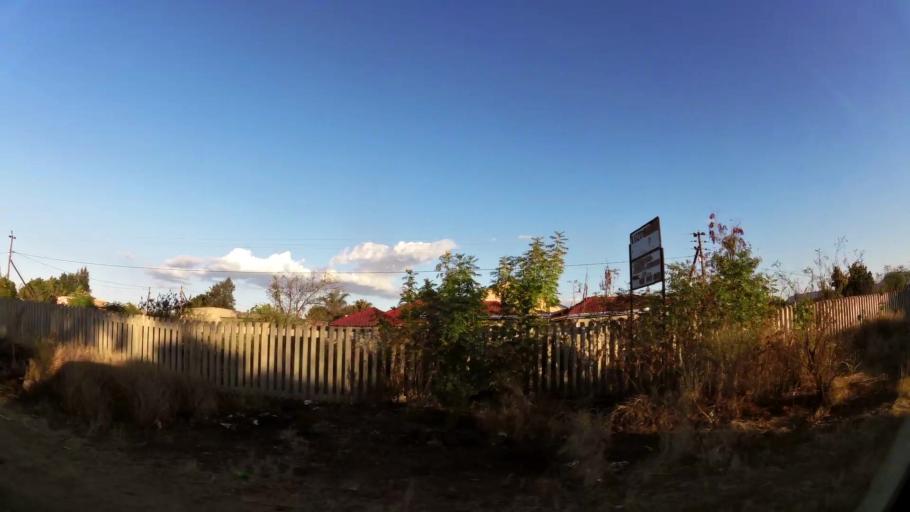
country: ZA
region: Limpopo
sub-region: Waterberg District Municipality
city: Mokopane
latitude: -24.1434
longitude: 28.9915
